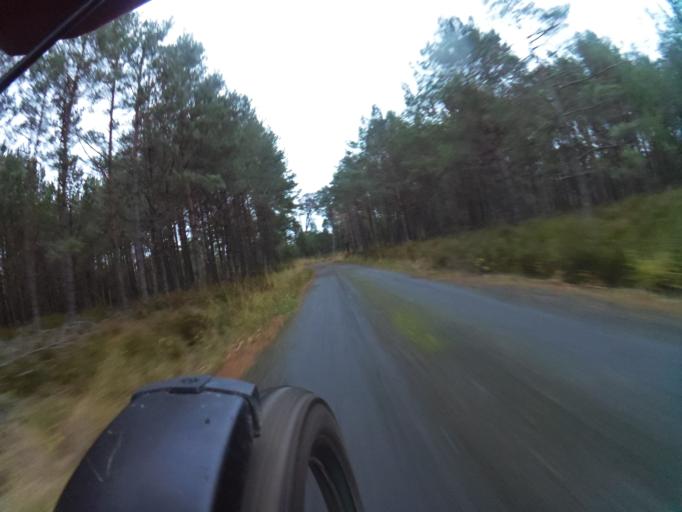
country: PL
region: Pomeranian Voivodeship
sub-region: Powiat wejherowski
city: Choczewo
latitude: 54.7967
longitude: 17.7793
